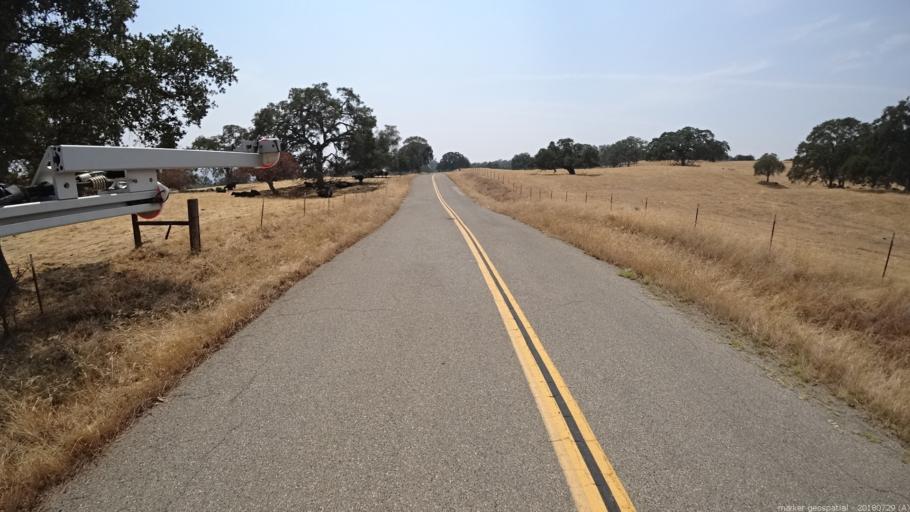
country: US
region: California
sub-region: Madera County
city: Yosemite Lakes
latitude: 37.2808
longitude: -119.8250
